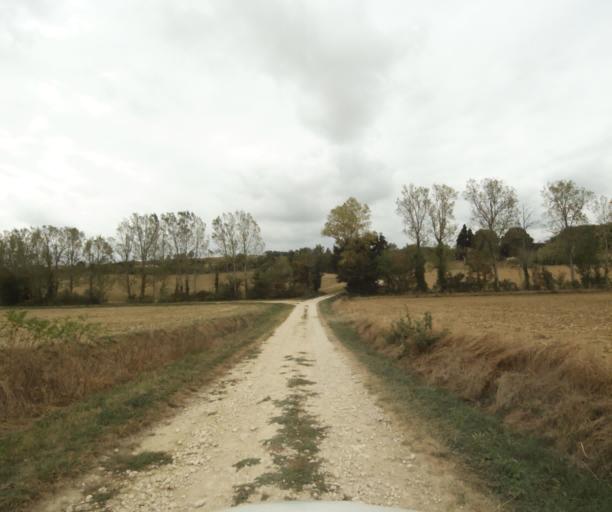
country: FR
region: Midi-Pyrenees
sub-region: Departement de la Haute-Garonne
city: Villefranche-de-Lauragais
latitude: 43.4163
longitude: 1.7463
